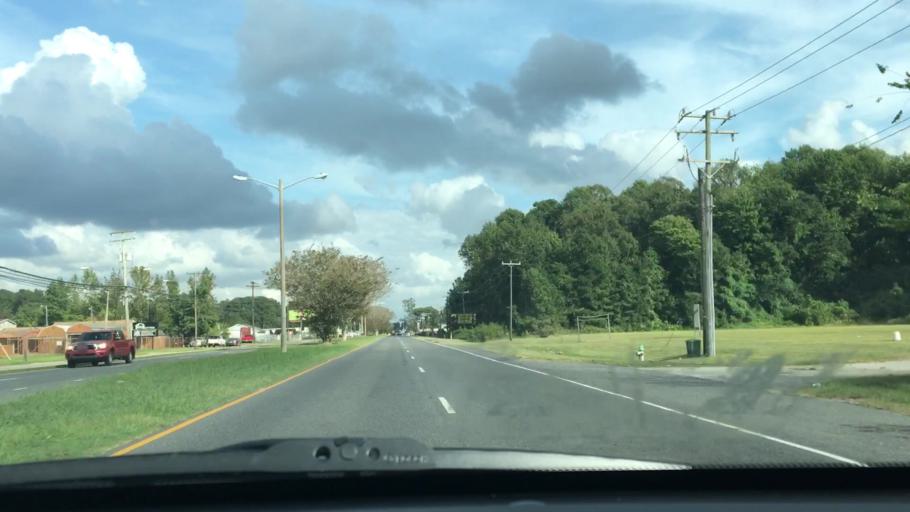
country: US
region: Virginia
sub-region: City of Portsmouth
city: Portsmouth Heights
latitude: 36.7726
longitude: -76.3331
